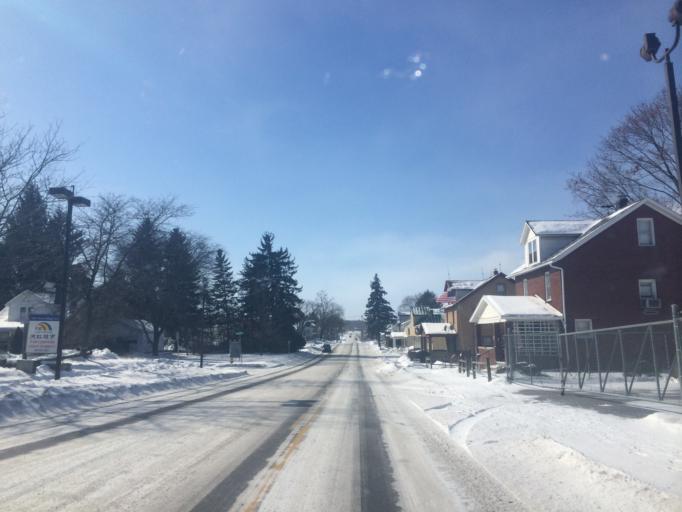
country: US
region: Pennsylvania
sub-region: Centre County
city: State College
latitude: 40.7859
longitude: -77.8728
